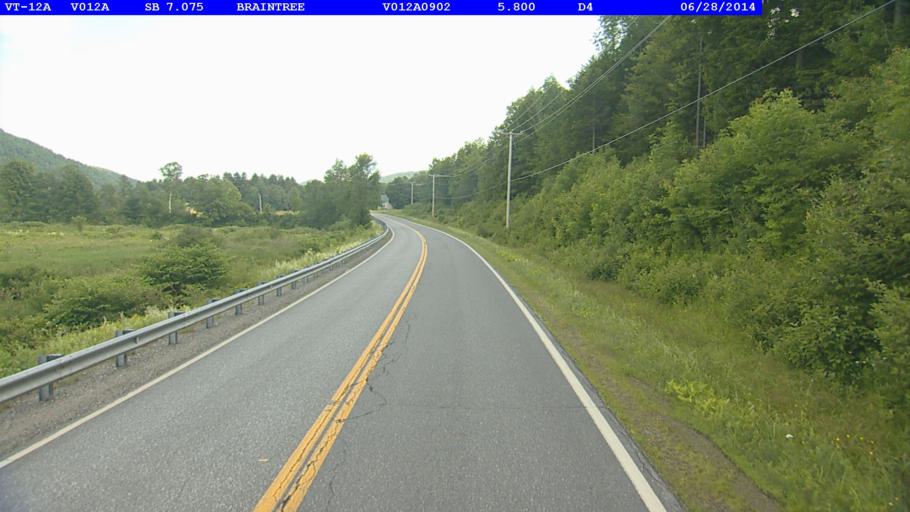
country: US
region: Vermont
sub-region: Orange County
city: Randolph
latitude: 43.9908
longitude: -72.7528
